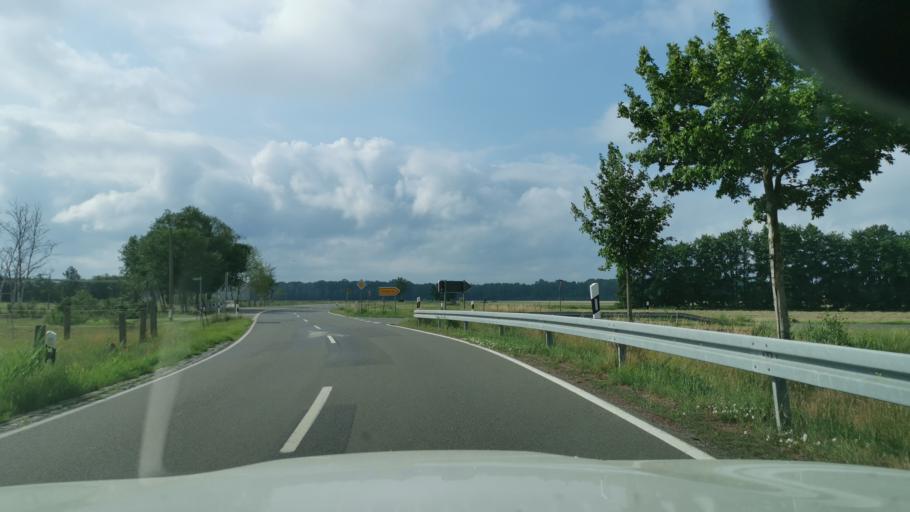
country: DE
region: Saxony-Anhalt
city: Annaburg
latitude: 51.7638
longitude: 13.0313
